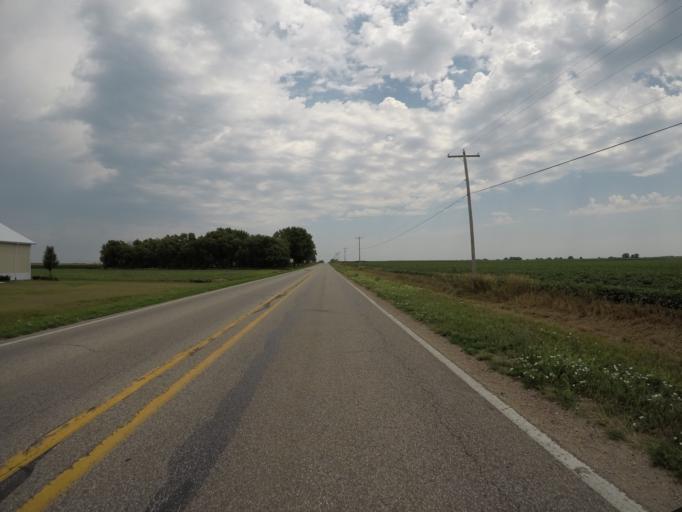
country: US
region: Nebraska
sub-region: Adams County
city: Hastings
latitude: 40.5971
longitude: -98.5008
